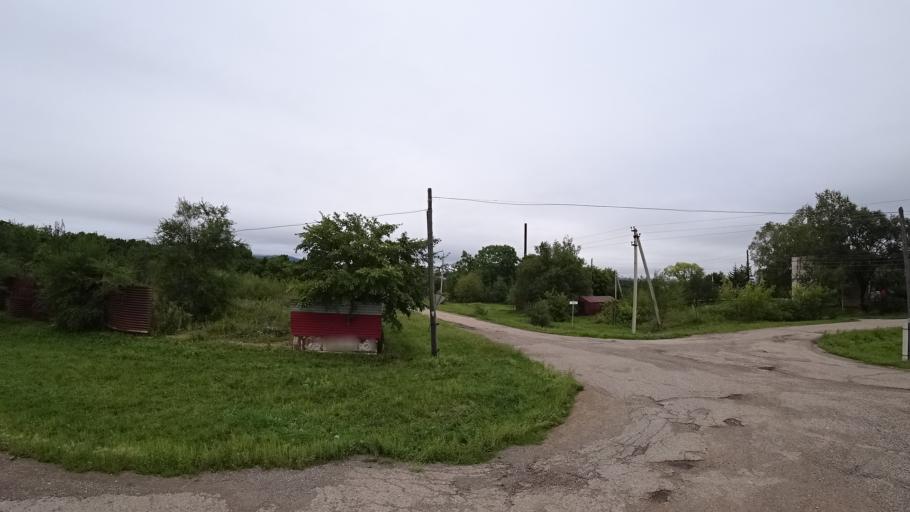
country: RU
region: Primorskiy
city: Monastyrishche
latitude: 44.0838
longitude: 132.5802
